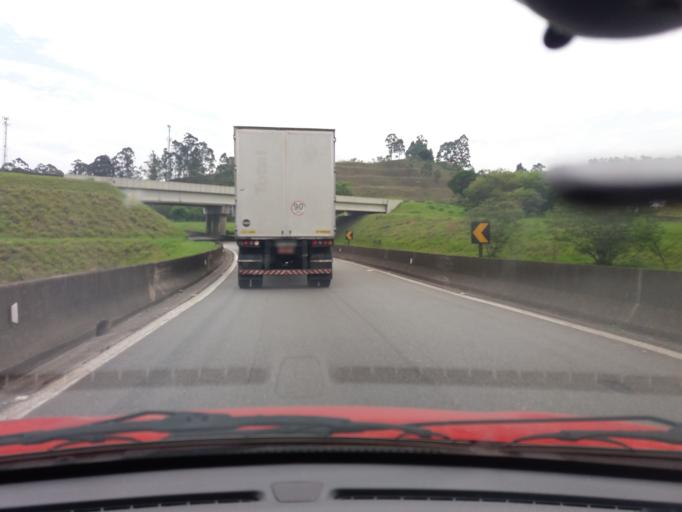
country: BR
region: Sao Paulo
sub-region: Caieiras
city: Caieiras
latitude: -23.4338
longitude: -46.7583
